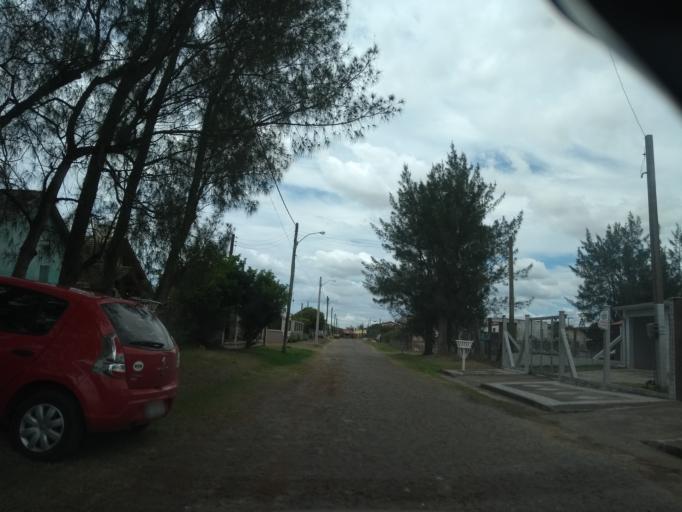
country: BR
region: Rio Grande do Sul
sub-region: Tramandai
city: Tramandai
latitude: -30.0663
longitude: -50.1621
